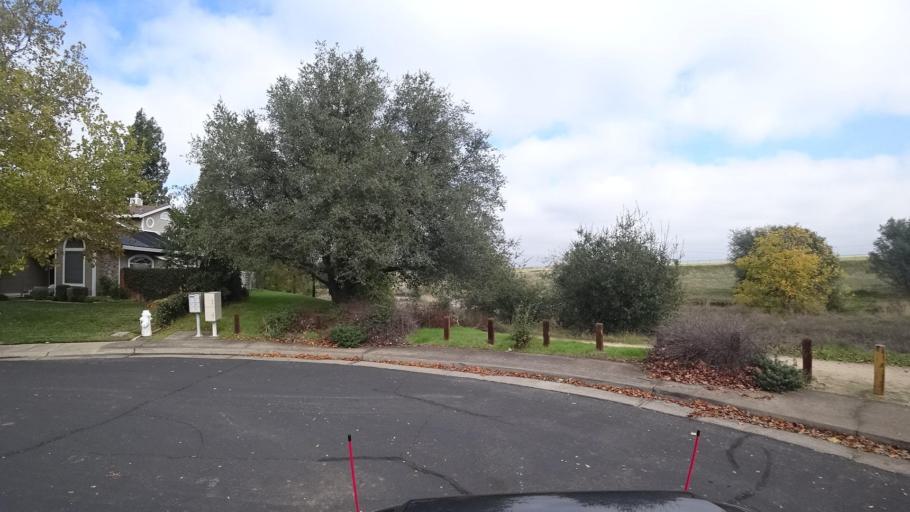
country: US
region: California
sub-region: Sacramento County
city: Elk Grove
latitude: 38.4186
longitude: -121.3570
